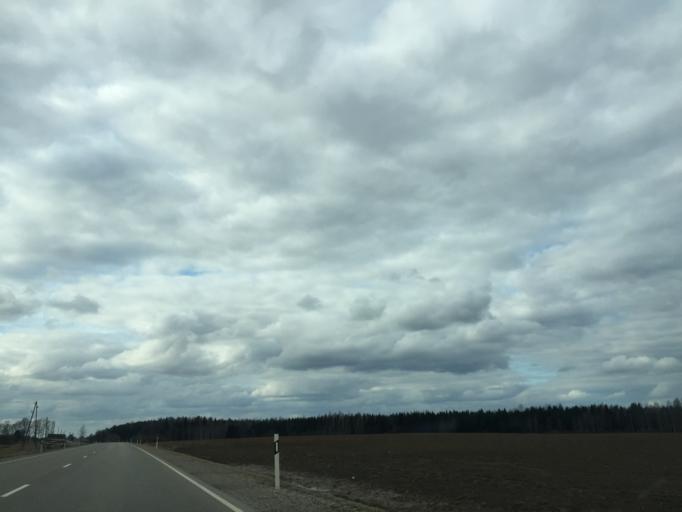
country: LV
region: Lielvarde
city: Lielvarde
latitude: 56.4939
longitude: 24.7645
